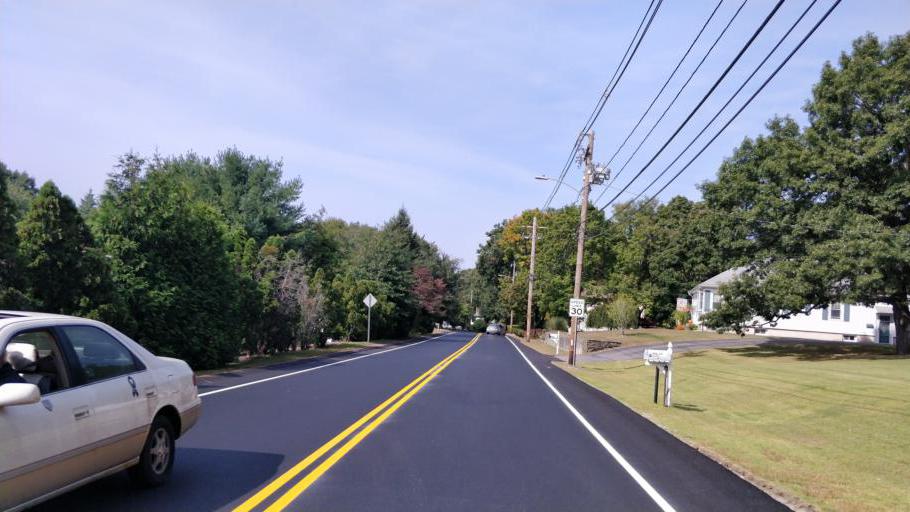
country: US
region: Massachusetts
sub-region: Bristol County
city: North Seekonk
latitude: 41.9046
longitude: -71.3214
